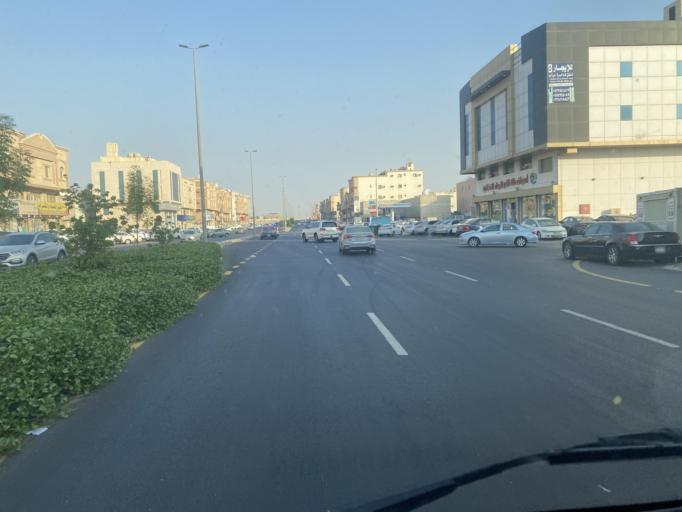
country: SA
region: Eastern Province
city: Dhahran
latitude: 26.3554
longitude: 50.0472
